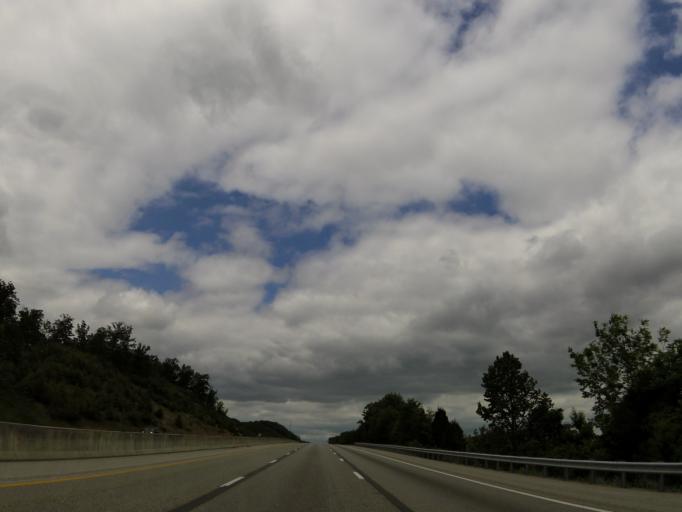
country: US
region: Kentucky
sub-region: Madison County
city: Berea
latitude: 37.4839
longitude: -84.3321
